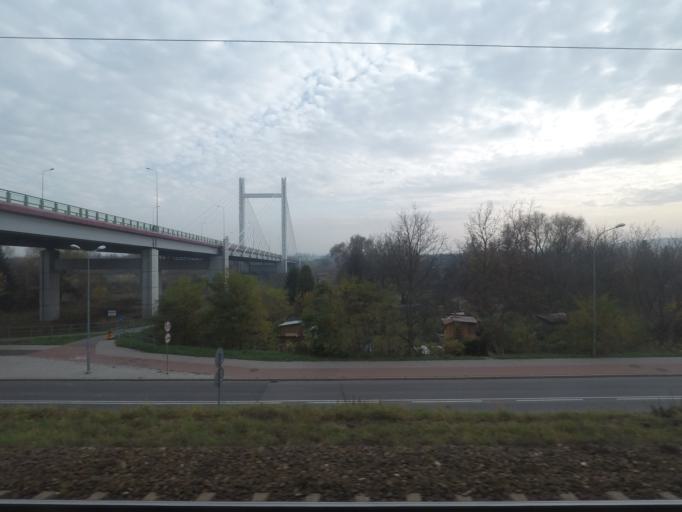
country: PL
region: Subcarpathian Voivodeship
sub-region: Przemysl
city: Przemysl
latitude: 49.7981
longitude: 22.7835
